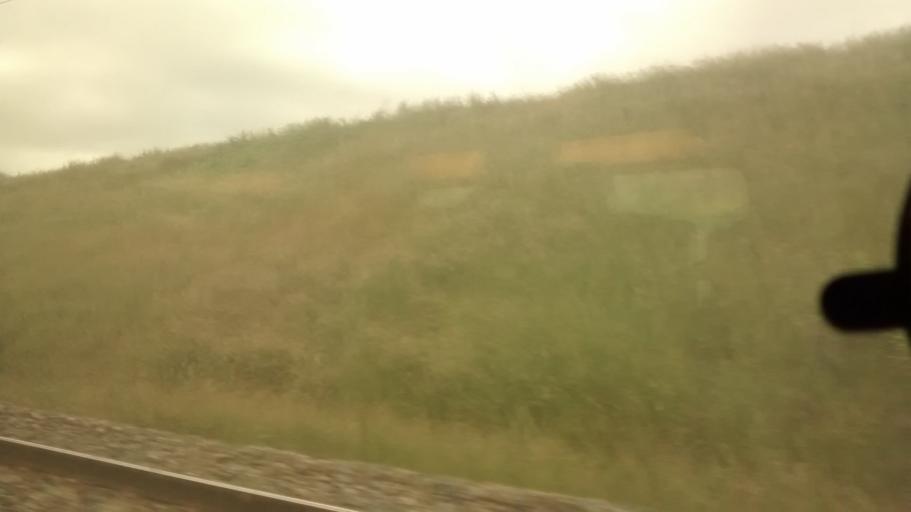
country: FR
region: Centre
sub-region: Departement d'Eure-et-Loir
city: Arrou
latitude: 48.0904
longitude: 1.1280
